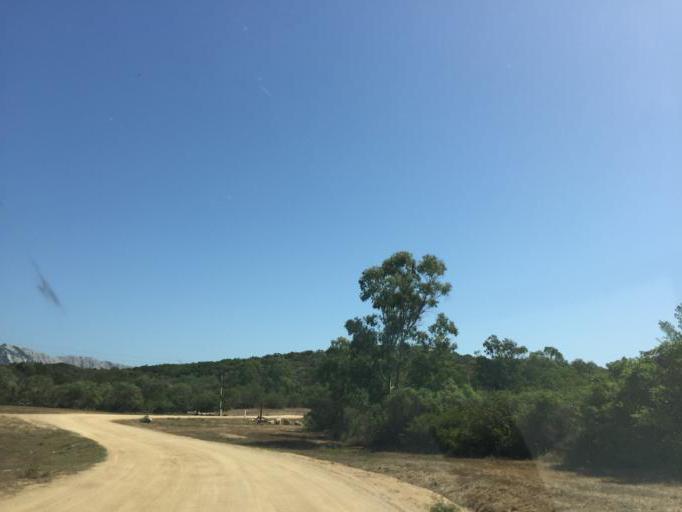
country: IT
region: Sardinia
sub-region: Provincia di Olbia-Tempio
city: San Teodoro
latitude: 40.8363
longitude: 9.6812
